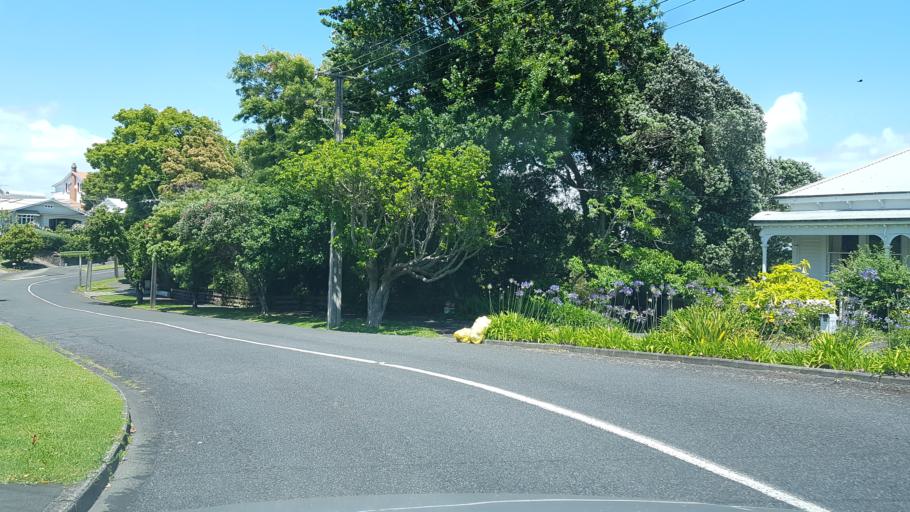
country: NZ
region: Auckland
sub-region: Auckland
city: North Shore
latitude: -36.8269
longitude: 174.7753
